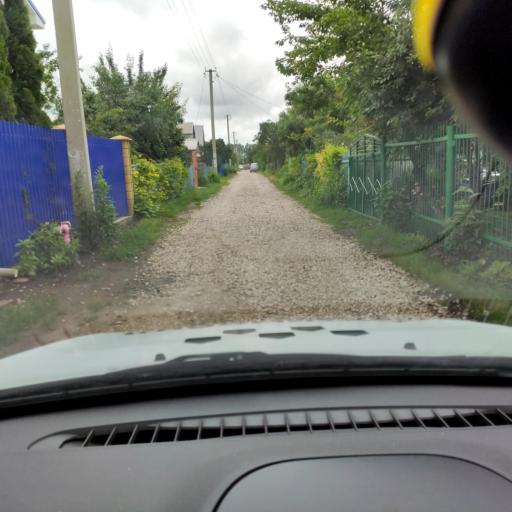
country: RU
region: Samara
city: Tol'yatti
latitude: 53.5957
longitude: 49.2899
